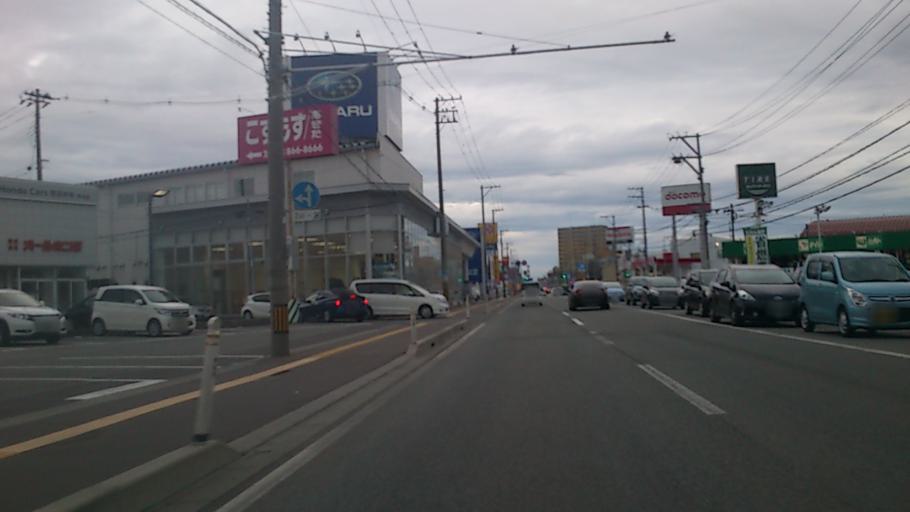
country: JP
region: Akita
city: Akita Shi
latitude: 39.7411
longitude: 140.0943
